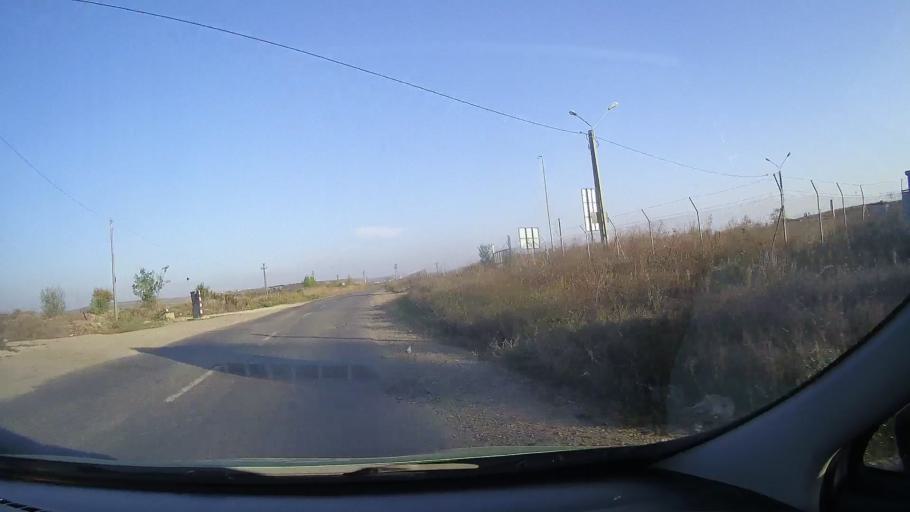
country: RO
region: Bihor
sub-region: Comuna Bors
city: Santion
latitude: 47.1129
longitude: 21.8565
